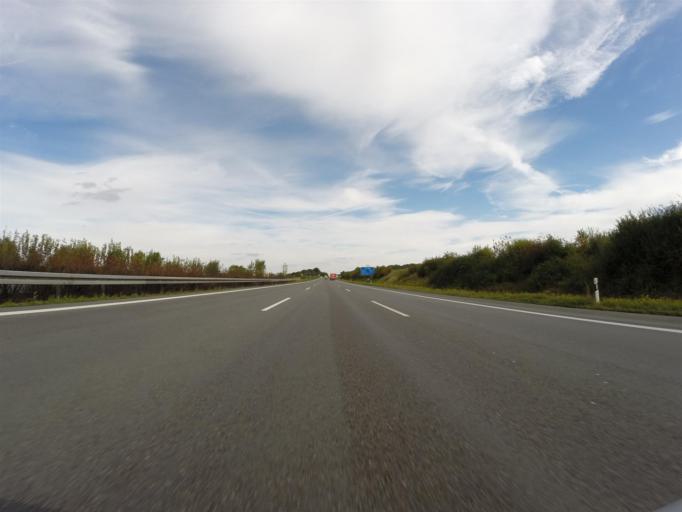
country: DE
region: Saxony
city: Nossen
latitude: 51.0424
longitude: 13.3335
